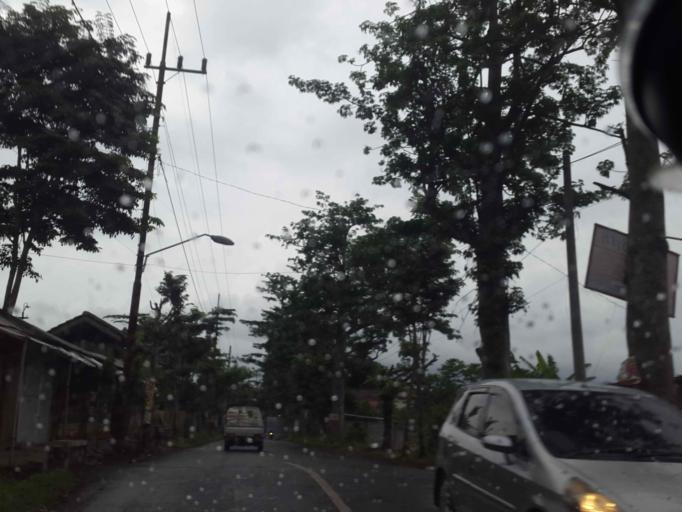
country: ID
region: East Java
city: Batu
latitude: -7.8634
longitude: 112.5314
